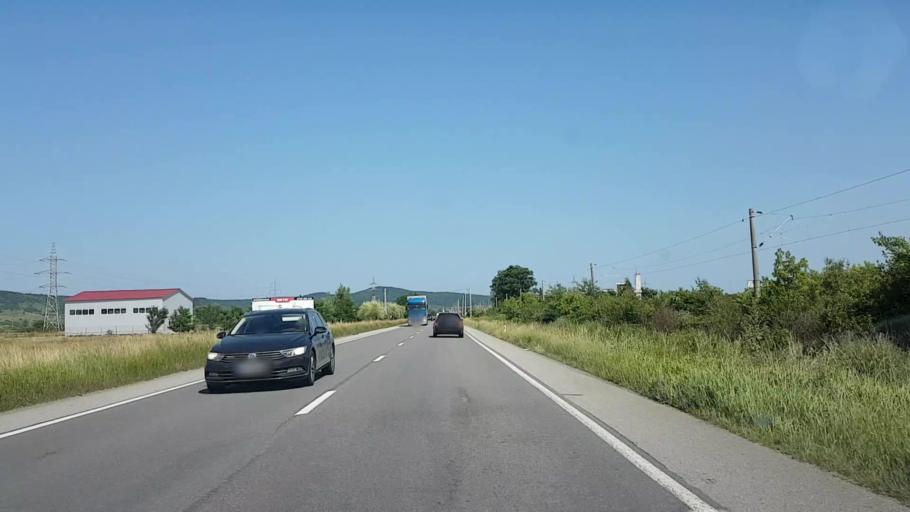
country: RO
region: Bistrita-Nasaud
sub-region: Comuna Sintereag
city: Cociu
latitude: 47.1815
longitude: 24.2549
